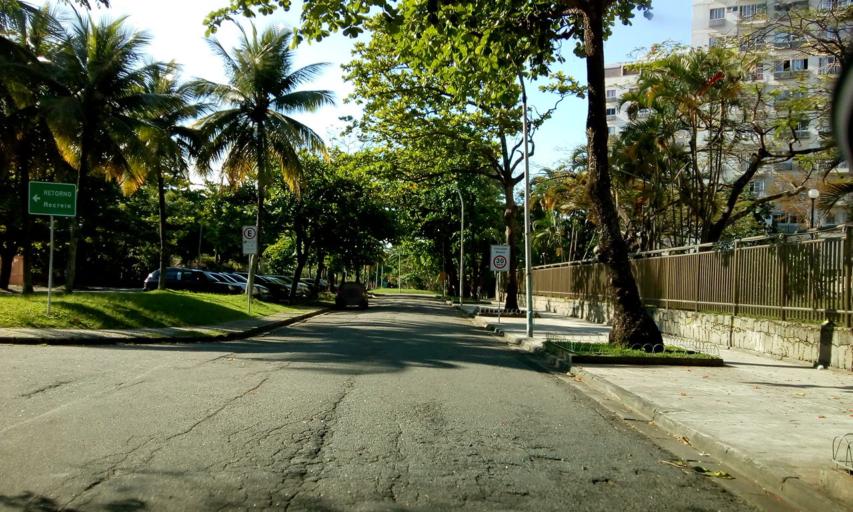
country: BR
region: Rio de Janeiro
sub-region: Nilopolis
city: Nilopolis
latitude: -22.9995
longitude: -43.3784
